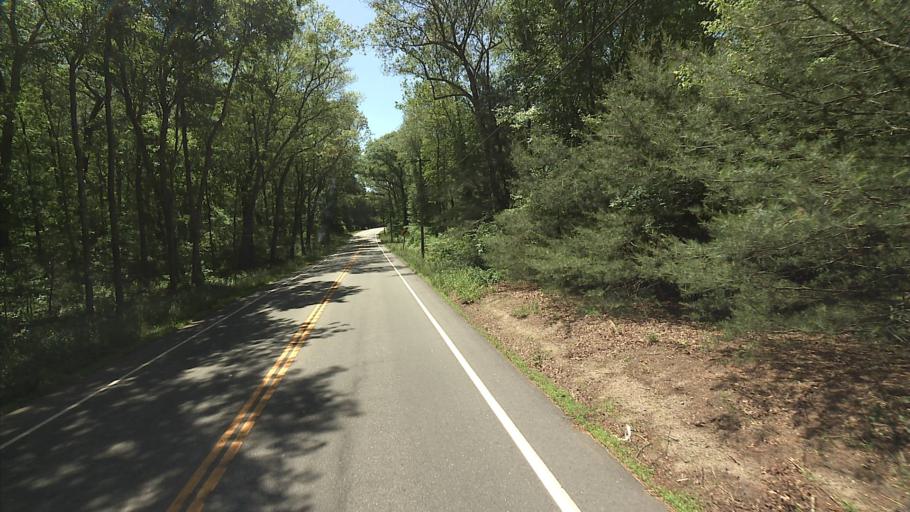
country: US
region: Rhode Island
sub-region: Washington County
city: Hopkinton
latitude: 41.5335
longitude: -71.8377
